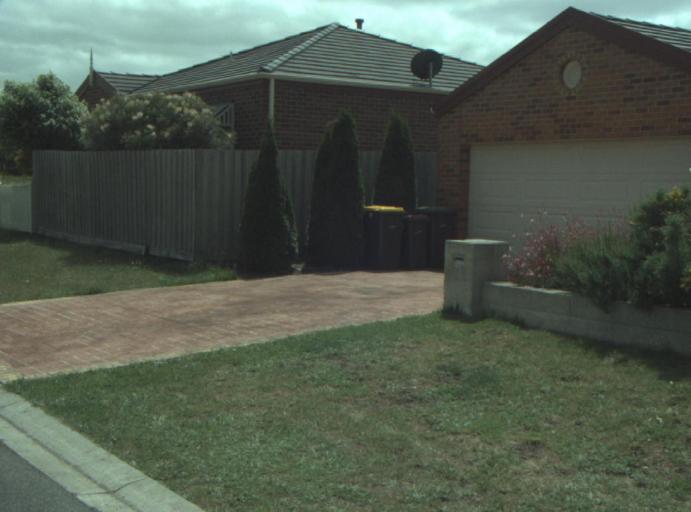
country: AU
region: Victoria
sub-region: Greater Geelong
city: Wandana Heights
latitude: -38.1941
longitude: 144.3084
